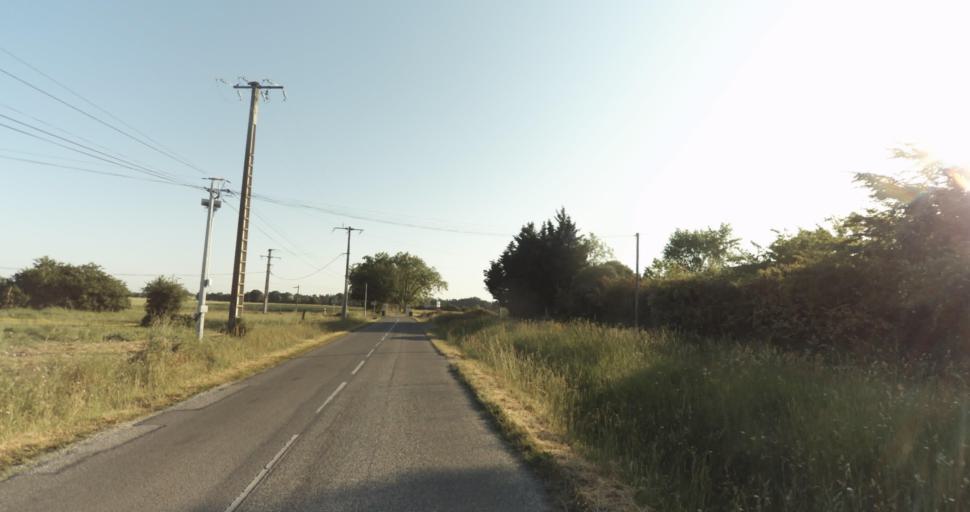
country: FR
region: Midi-Pyrenees
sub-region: Departement de la Haute-Garonne
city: Leguevin
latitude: 43.5751
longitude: 1.2369
